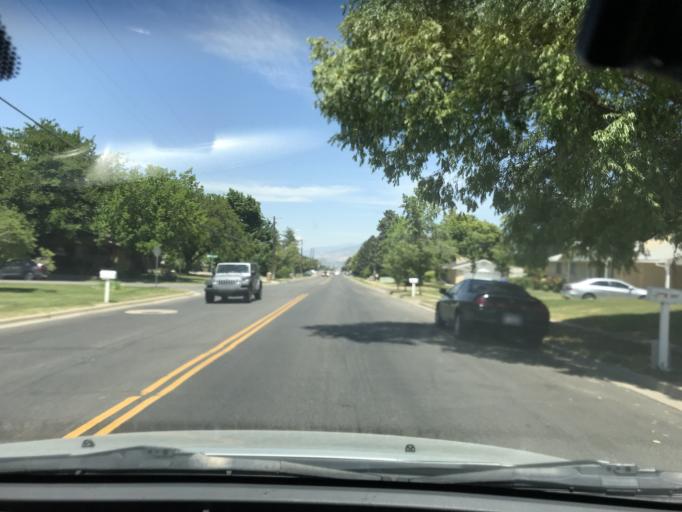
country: US
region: Utah
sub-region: Davis County
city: Woods Cross
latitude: 40.8580
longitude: -111.8922
